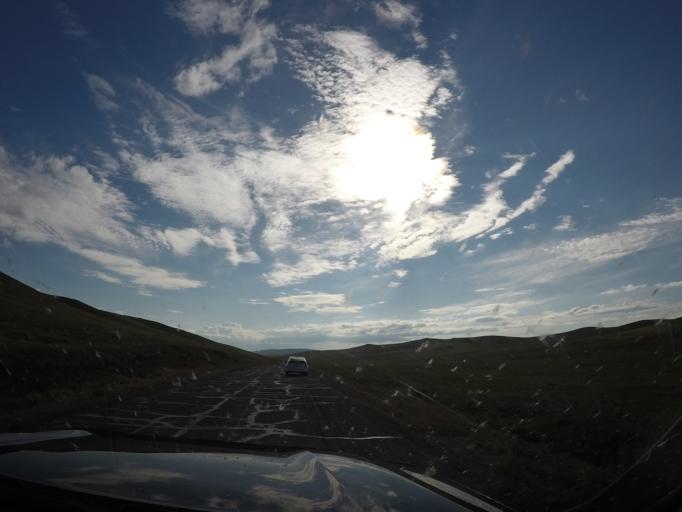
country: MN
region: Hentiy
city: Modot
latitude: 47.7905
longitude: 108.6786
